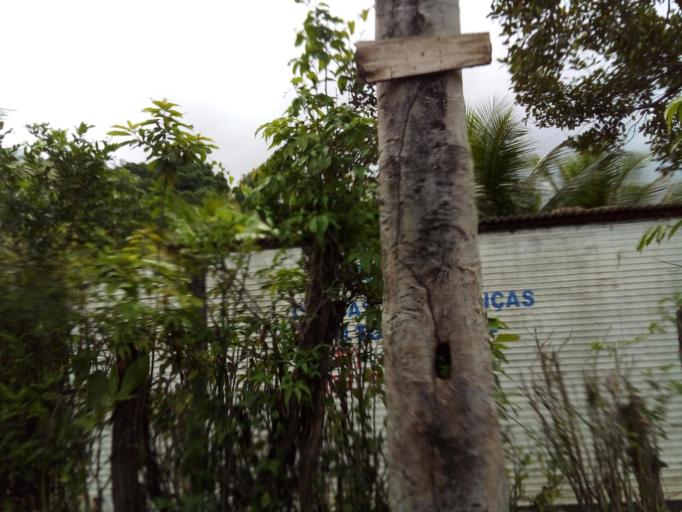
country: BR
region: Espirito Santo
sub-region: Joao Neiva
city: Joao Neiva
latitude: -19.7442
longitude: -40.3654
